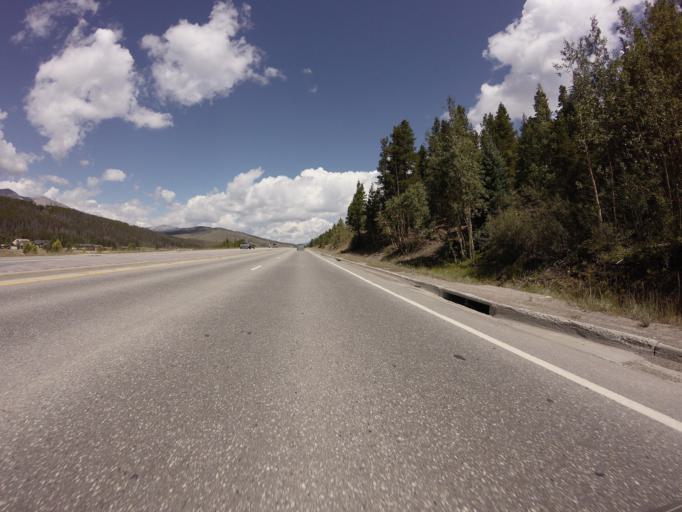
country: US
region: Colorado
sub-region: Summit County
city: Breckenridge
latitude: 39.5019
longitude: -106.0471
